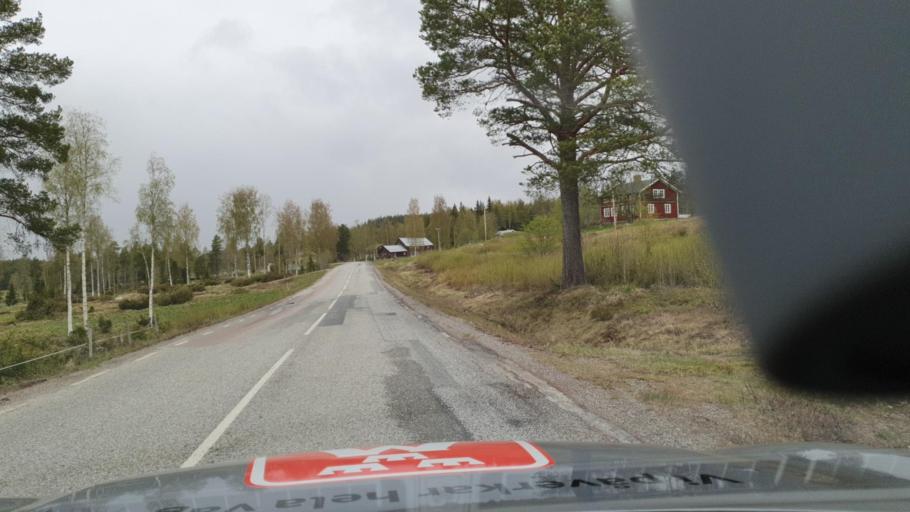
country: SE
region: Vaesterbotten
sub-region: Asele Kommun
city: Asele
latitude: 63.6824
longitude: 17.2481
